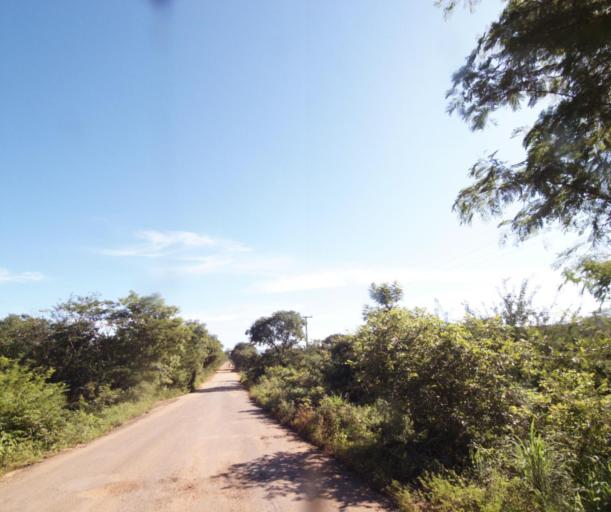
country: BR
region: Bahia
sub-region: Sao Felix Do Coribe
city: Santa Maria da Vitoria
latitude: -13.6462
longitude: -44.4423
